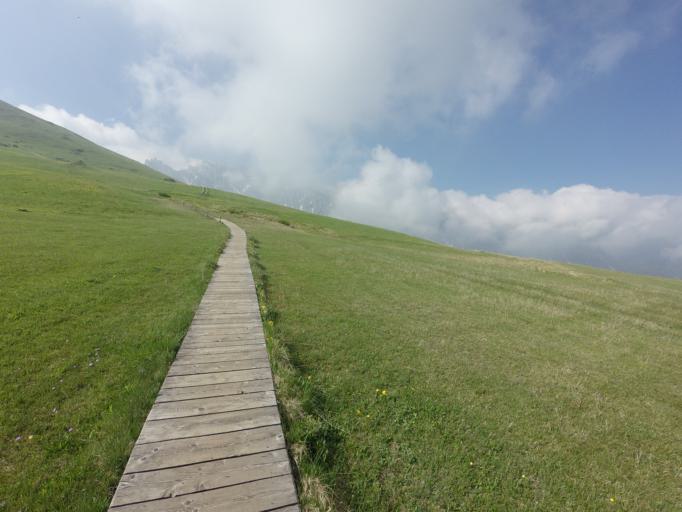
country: IT
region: Trentino-Alto Adige
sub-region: Bolzano
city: Ortisei
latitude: 46.5218
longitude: 11.6319
